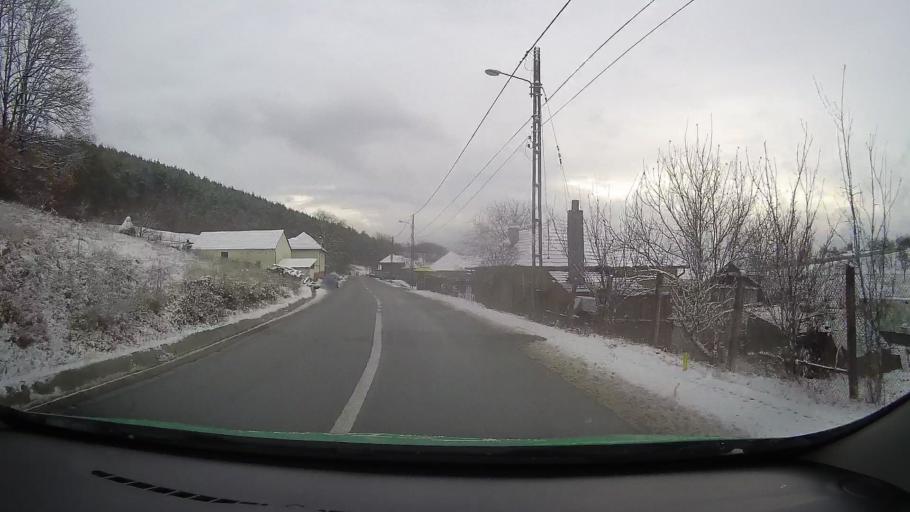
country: RO
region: Hunedoara
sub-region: Oras Hateg
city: Hateg
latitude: 45.6269
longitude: 22.9333
